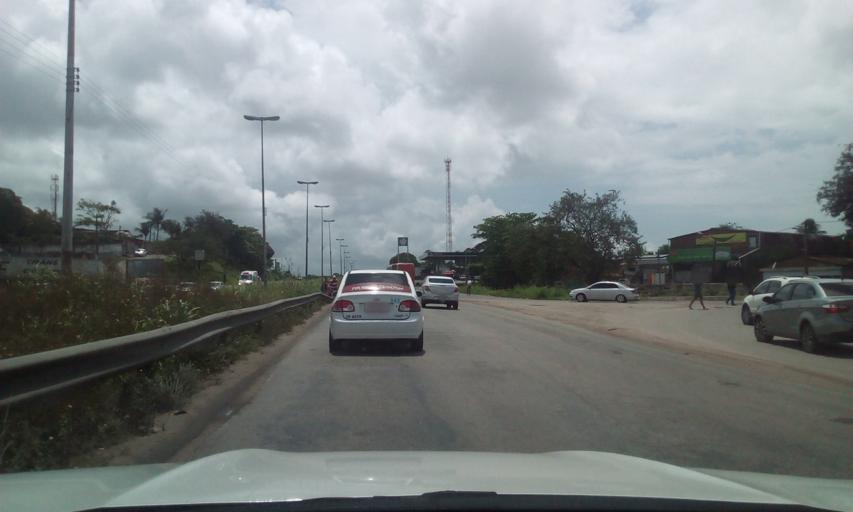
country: BR
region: Pernambuco
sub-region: Recife
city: Recife
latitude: -8.0803
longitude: -34.9431
